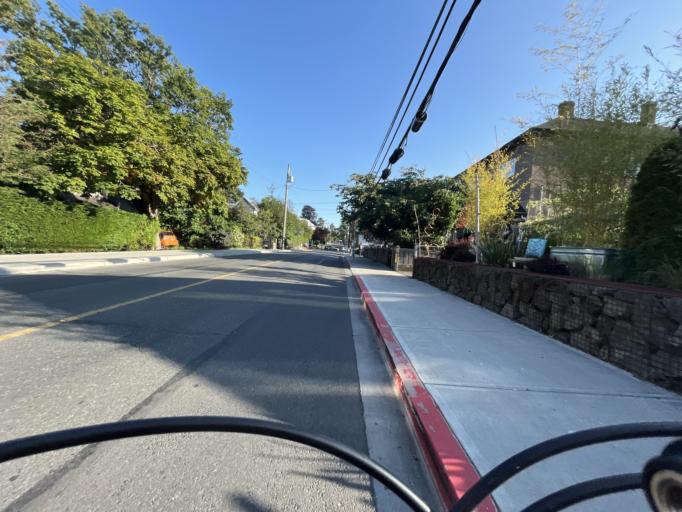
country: CA
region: British Columbia
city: Victoria
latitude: 48.4277
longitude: -123.3454
